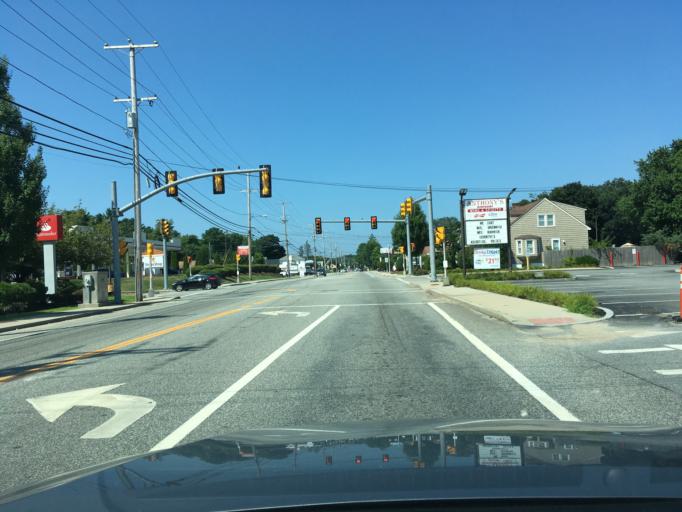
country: US
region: Rhode Island
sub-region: Kent County
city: West Warwick
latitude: 41.6807
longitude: -71.5694
